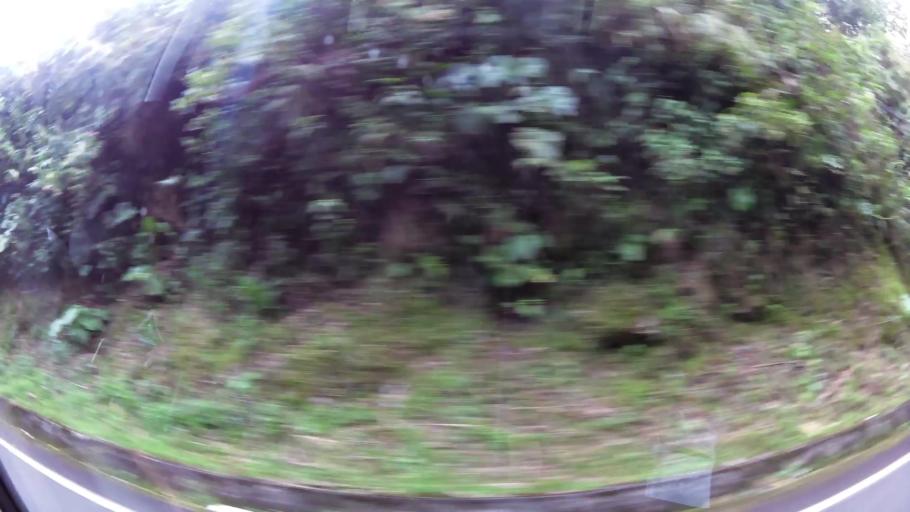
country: EC
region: Pastaza
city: Puyo
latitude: -1.4345
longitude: -78.1777
